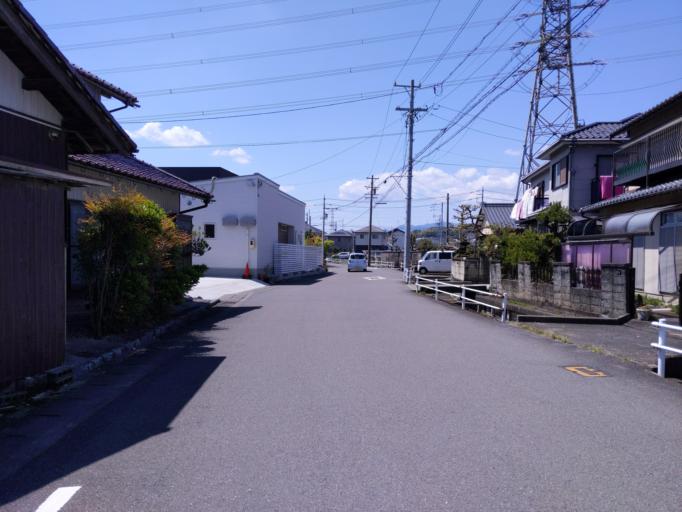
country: JP
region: Gifu
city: Godo
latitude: 35.3929
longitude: 136.5928
